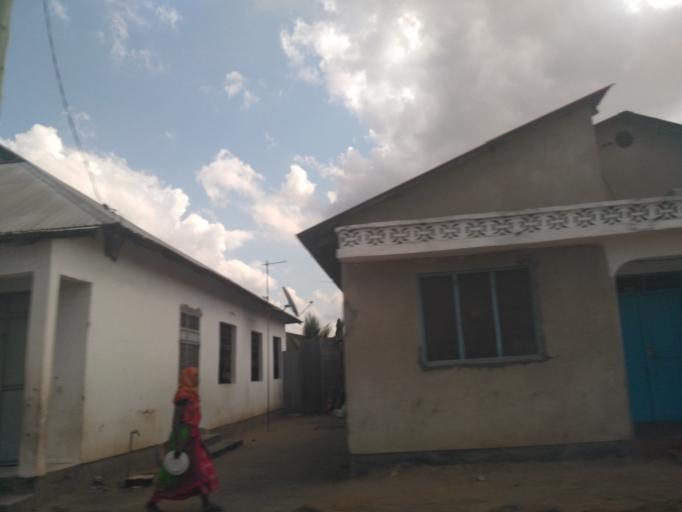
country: TZ
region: Dar es Salaam
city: Dar es Salaam
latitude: -6.8965
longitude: 39.2821
